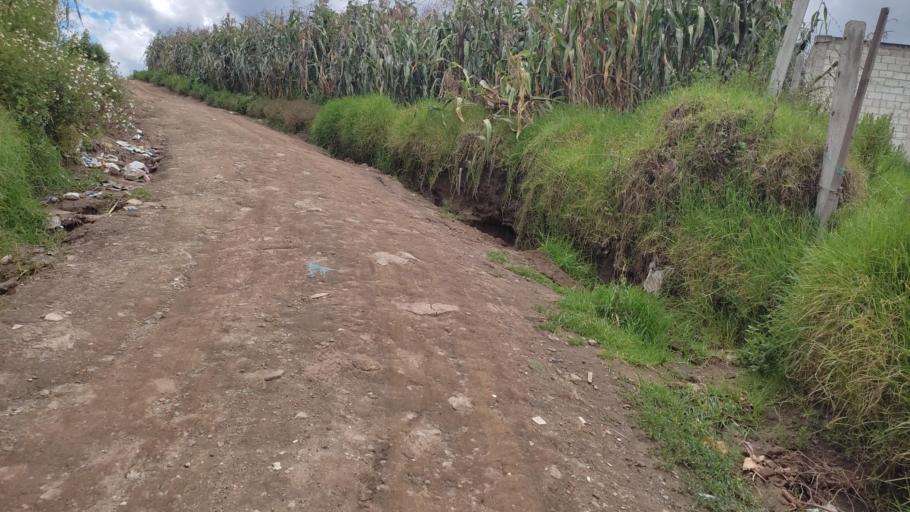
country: GT
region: Quetzaltenango
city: Quetzaltenango
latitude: 14.8588
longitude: -91.5296
